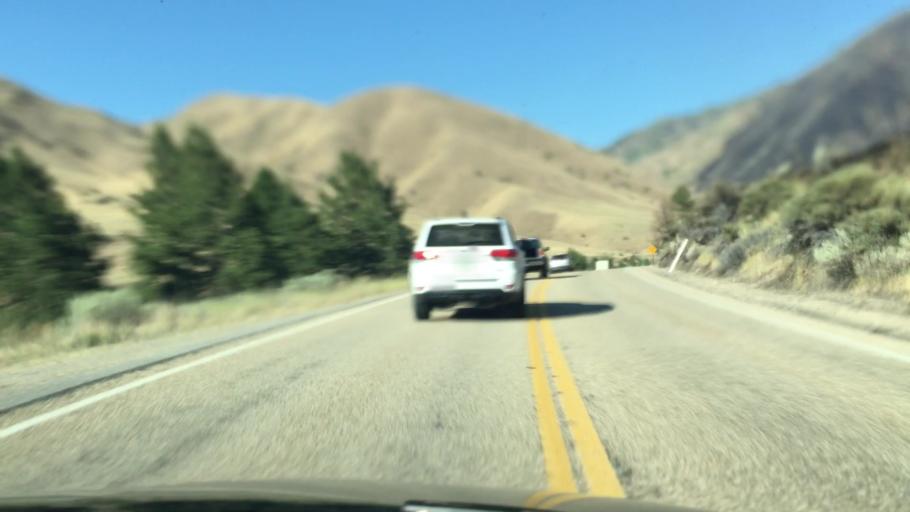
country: US
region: Idaho
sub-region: Gem County
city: Emmett
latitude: 44.0062
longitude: -116.1788
